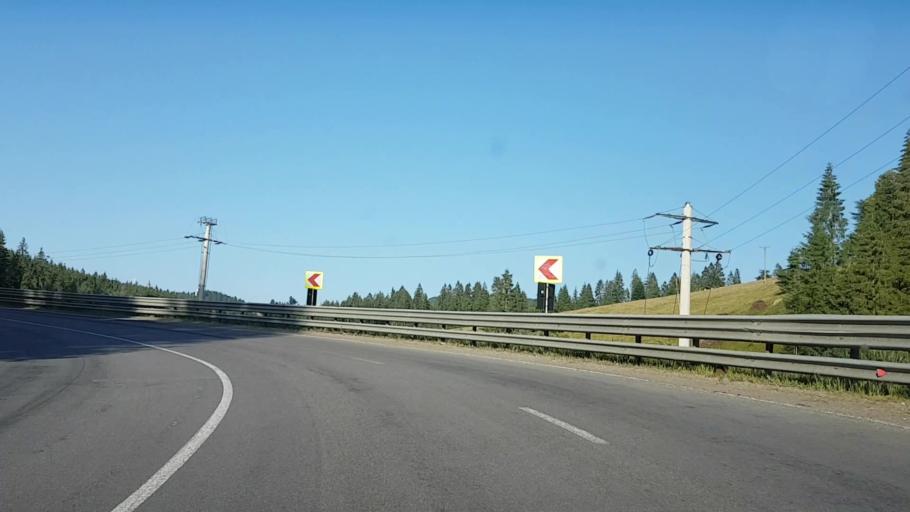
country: RO
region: Bistrita-Nasaud
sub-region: Comuna Lunca Ilvei
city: Lunca Ilvei
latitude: 47.2269
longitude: 24.9754
